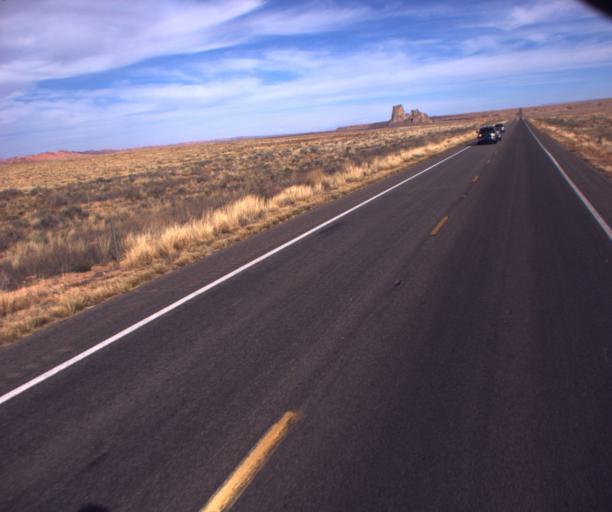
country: US
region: Arizona
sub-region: Navajo County
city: Kayenta
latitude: 36.7208
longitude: -110.1622
